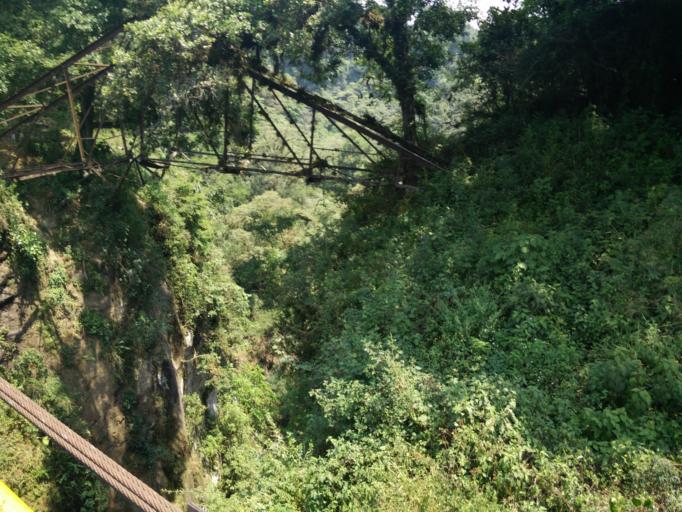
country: MX
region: Veracruz
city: Xico
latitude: 19.4022
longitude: -96.9944
